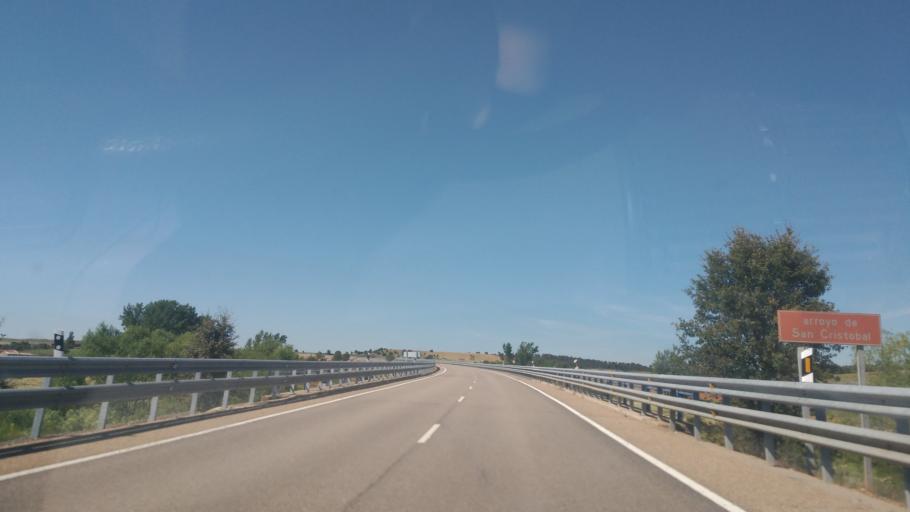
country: ES
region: Castille and Leon
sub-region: Provincia de Zamora
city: Cuelgamures
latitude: 41.2516
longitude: -5.7038
